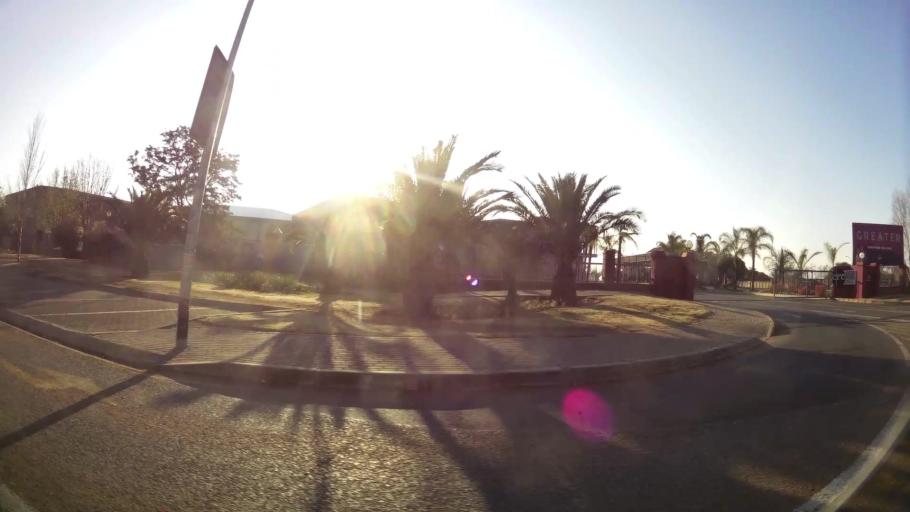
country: ZA
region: Orange Free State
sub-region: Mangaung Metropolitan Municipality
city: Bloemfontein
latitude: -29.1614
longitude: 26.1904
